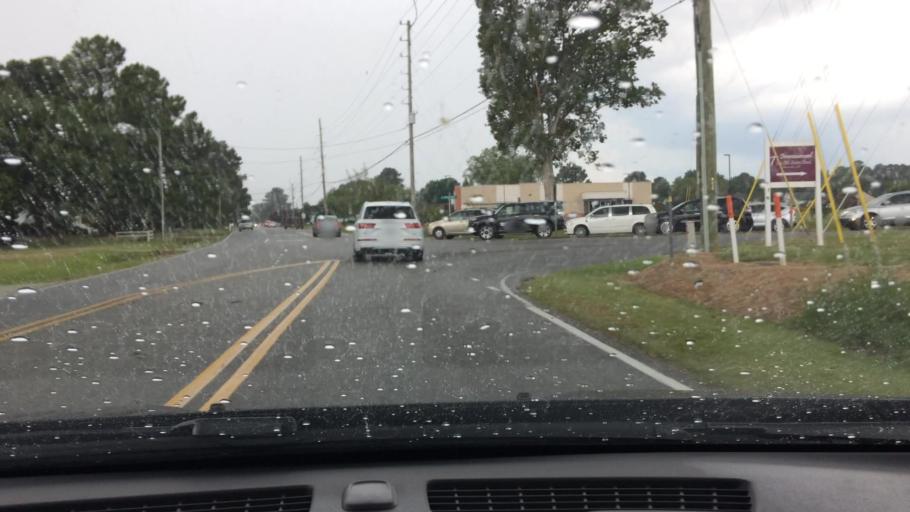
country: US
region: North Carolina
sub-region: Pitt County
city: Winterville
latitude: 35.5367
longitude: -77.3852
